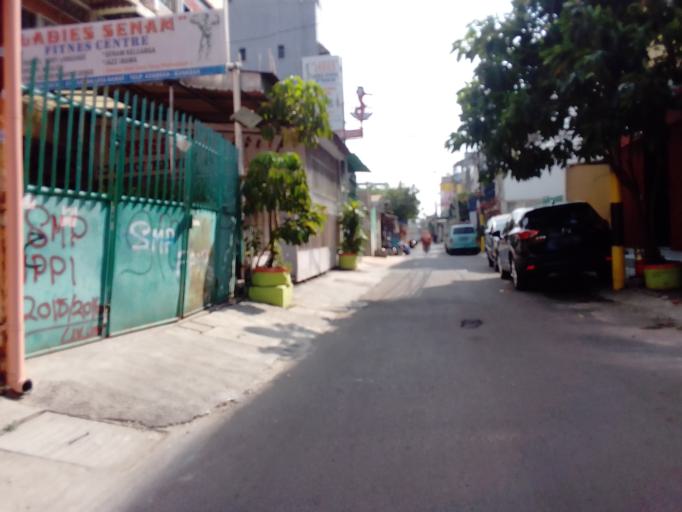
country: ID
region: Jakarta Raya
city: Jakarta
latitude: -6.1507
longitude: 106.8159
